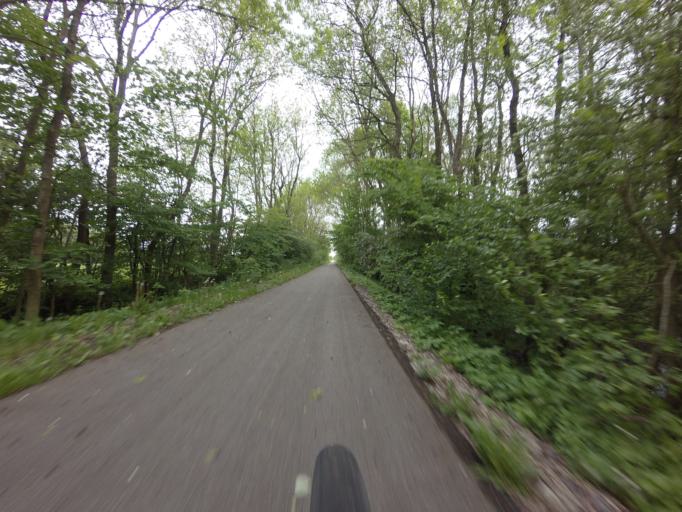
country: DK
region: Zealand
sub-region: Slagelse Kommune
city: Slagelse
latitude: 55.3172
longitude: 11.4082
